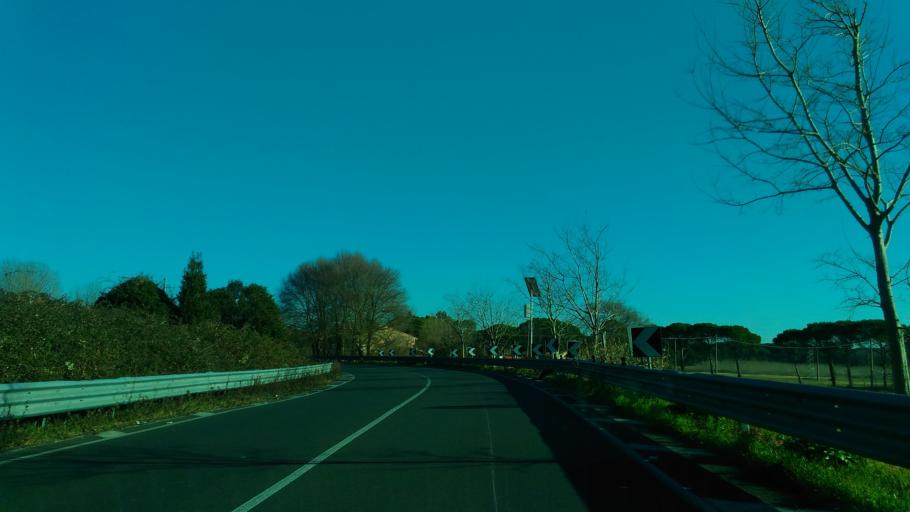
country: IT
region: Tuscany
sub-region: Province of Pisa
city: Marina di Pisa
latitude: 43.6754
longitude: 10.3177
